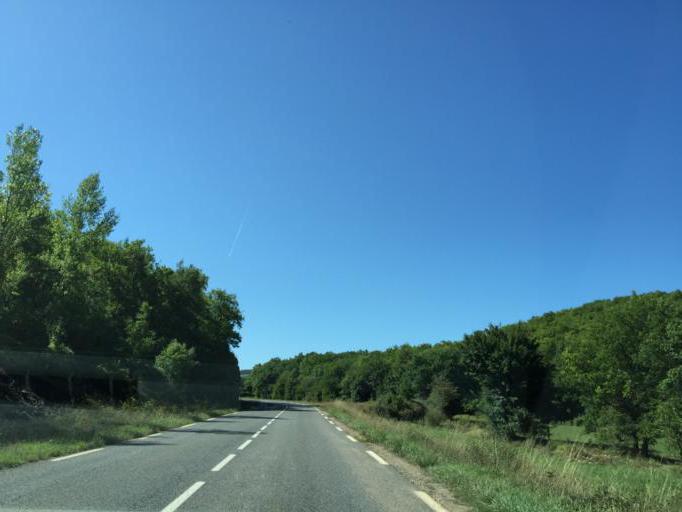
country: FR
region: Midi-Pyrenees
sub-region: Departement de l'Aveyron
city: Saint-Georges-de-Luzencon
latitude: 44.0194
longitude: 2.9358
